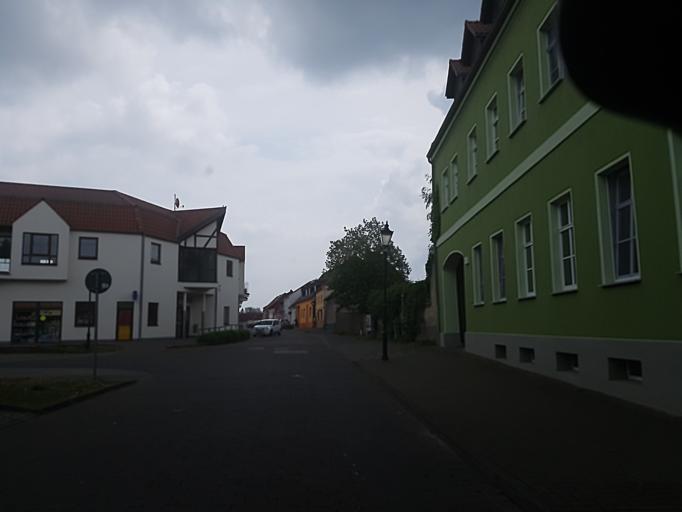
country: DE
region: Saxony-Anhalt
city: Loburg
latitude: 52.1153
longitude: 12.0740
